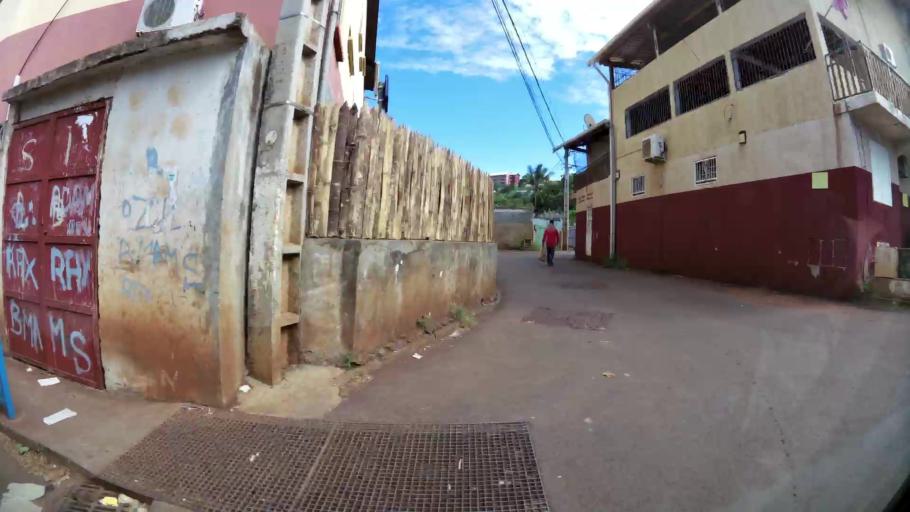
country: YT
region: Mamoudzou
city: Mamoudzou
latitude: -12.7828
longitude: 45.2199
